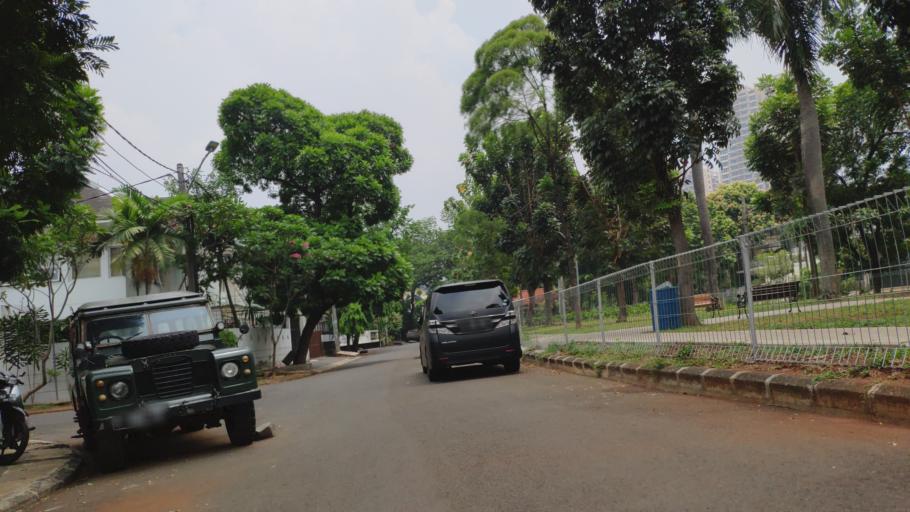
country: ID
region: Banten
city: South Tangerang
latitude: -6.2686
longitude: 106.7779
